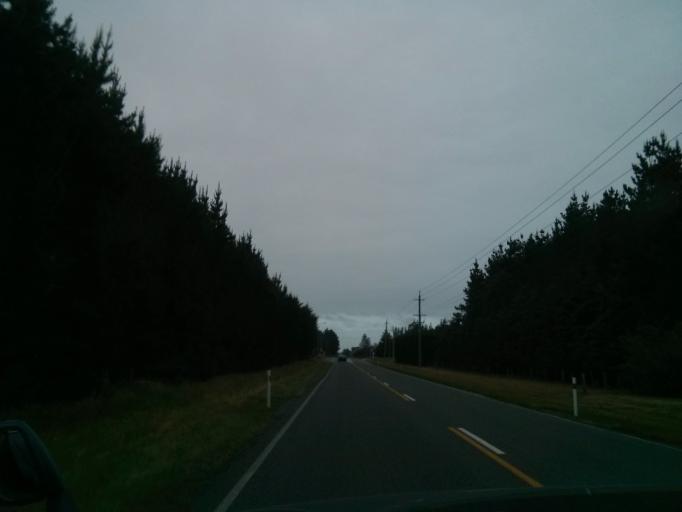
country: NZ
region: Canterbury
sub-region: Waimakariri District
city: Kaiapoi
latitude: -43.3784
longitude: 172.5312
